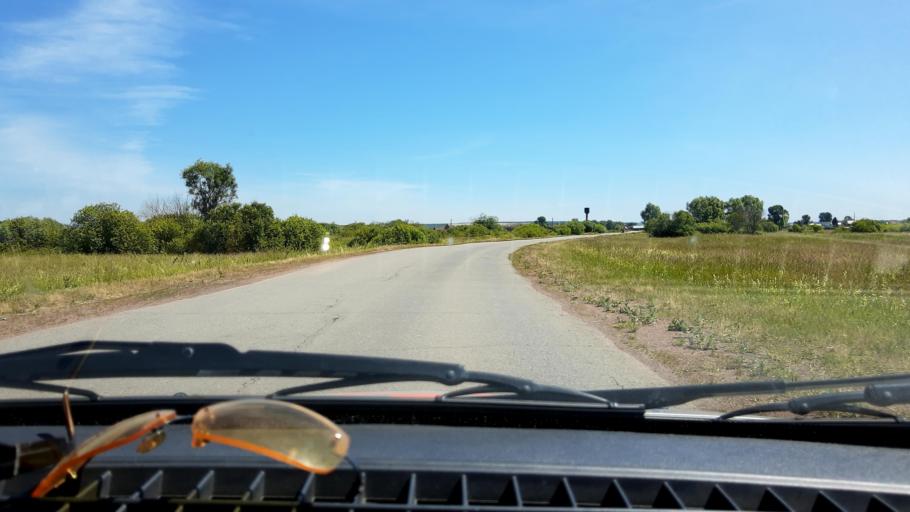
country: RU
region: Bashkortostan
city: Mikhaylovka
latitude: 54.9754
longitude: 55.7808
